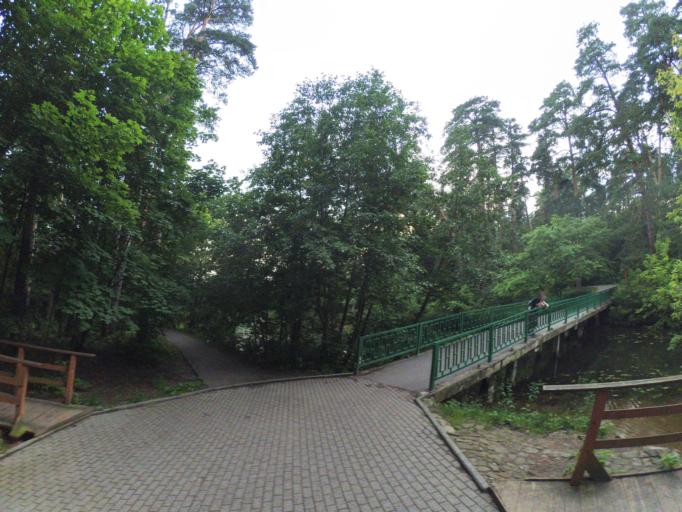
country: RU
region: Moscow
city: Shchukino
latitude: 55.7808
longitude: 37.4272
